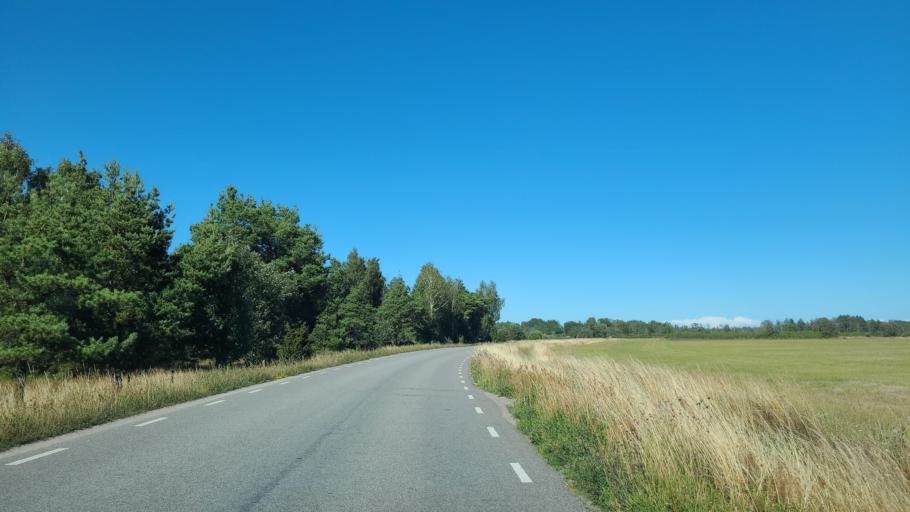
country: SE
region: Kalmar
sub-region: Borgholms Kommun
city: Borgholm
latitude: 56.9238
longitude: 16.8418
